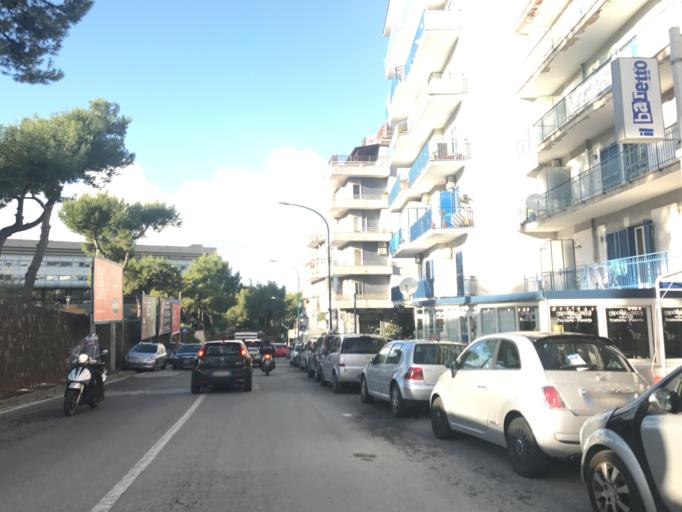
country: IT
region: Campania
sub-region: Provincia di Napoli
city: Napoli
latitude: 40.8687
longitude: 14.2228
